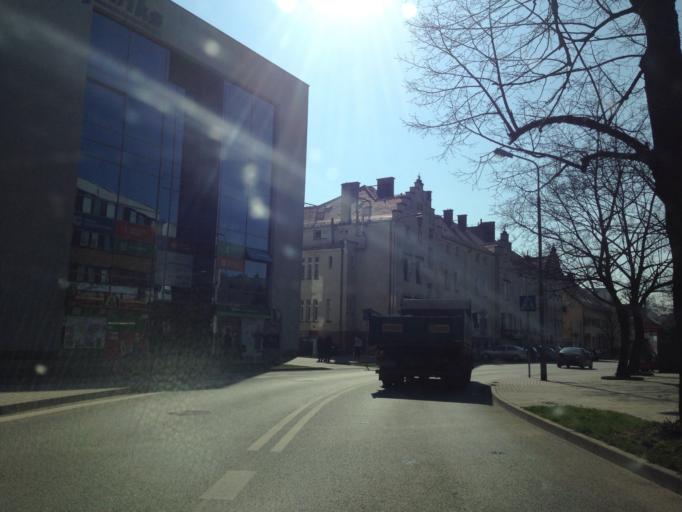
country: PL
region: Lower Silesian Voivodeship
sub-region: Powiat olesnicki
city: Olesnica
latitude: 51.2094
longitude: 17.3898
